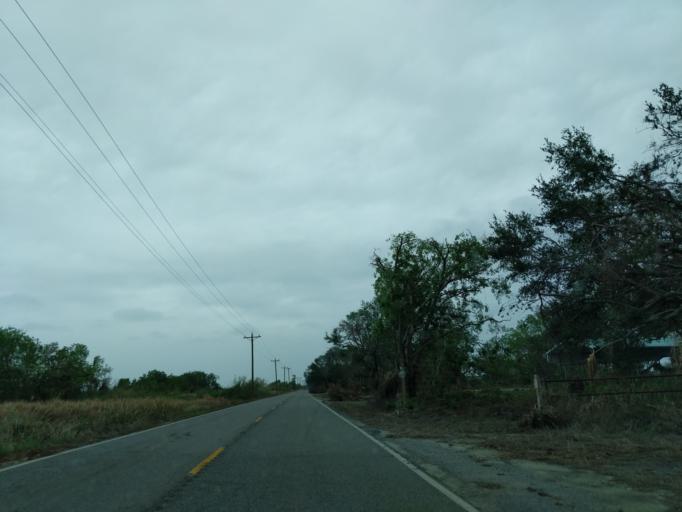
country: US
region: Louisiana
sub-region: Jefferson Davis Parish
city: Lake Arthur
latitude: 29.7530
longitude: -92.9130
